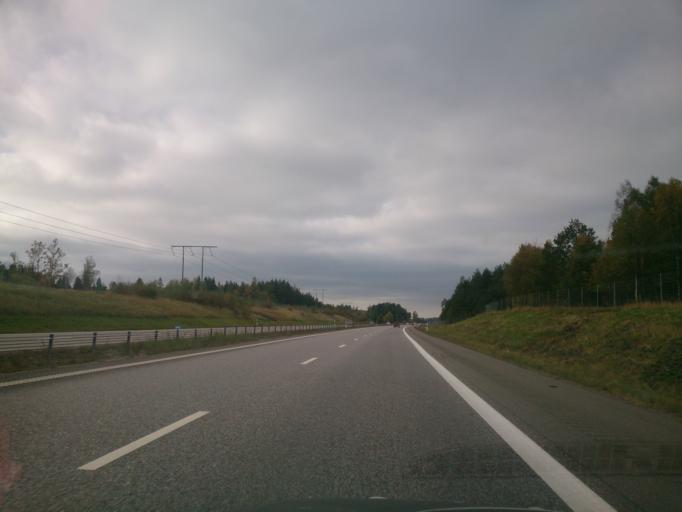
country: SE
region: OEstergoetland
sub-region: Norrkopings Kommun
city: Skarblacka
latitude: 58.4823
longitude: 15.8899
